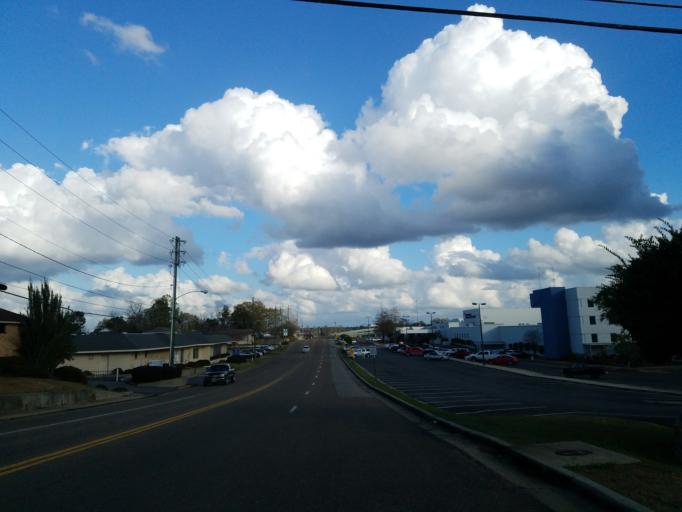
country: US
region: Mississippi
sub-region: Jones County
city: Laurel
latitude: 31.6859
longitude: -89.1427
